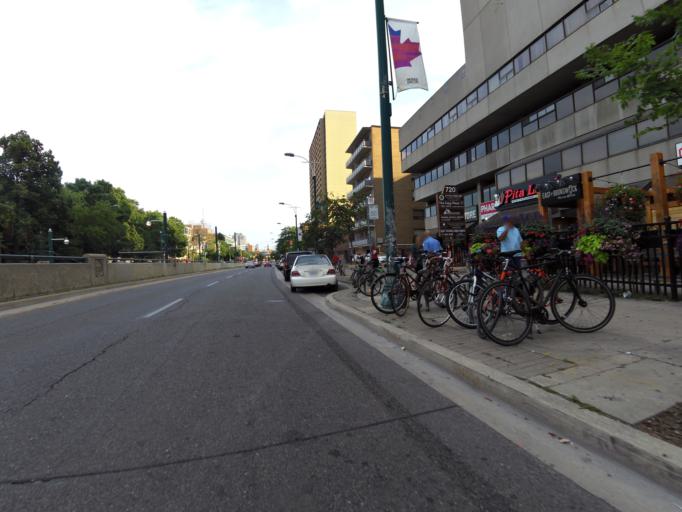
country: CA
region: Ontario
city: Toronto
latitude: 43.6657
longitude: -79.4033
